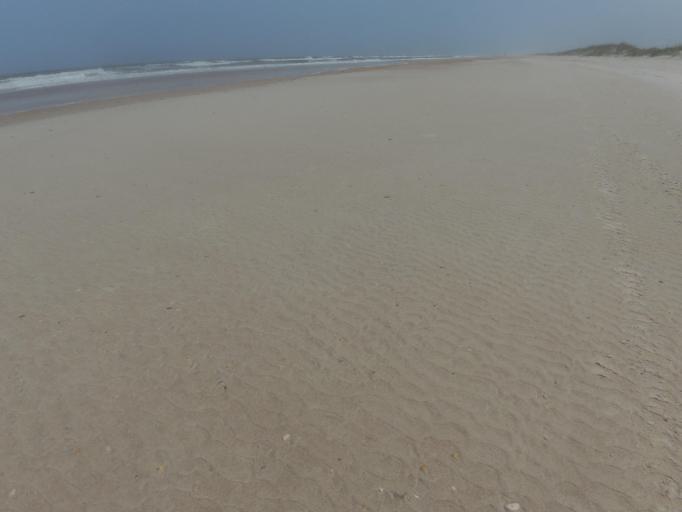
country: US
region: Florida
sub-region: Saint Johns County
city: Saint Augustine
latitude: 29.8926
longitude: -81.2754
